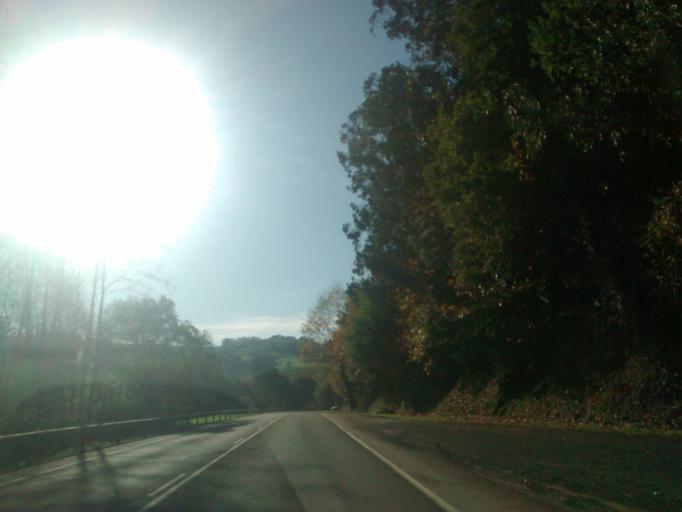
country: ES
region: Cantabria
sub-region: Provincia de Cantabria
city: Puente Viesgo
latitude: 43.3135
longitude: -3.9594
